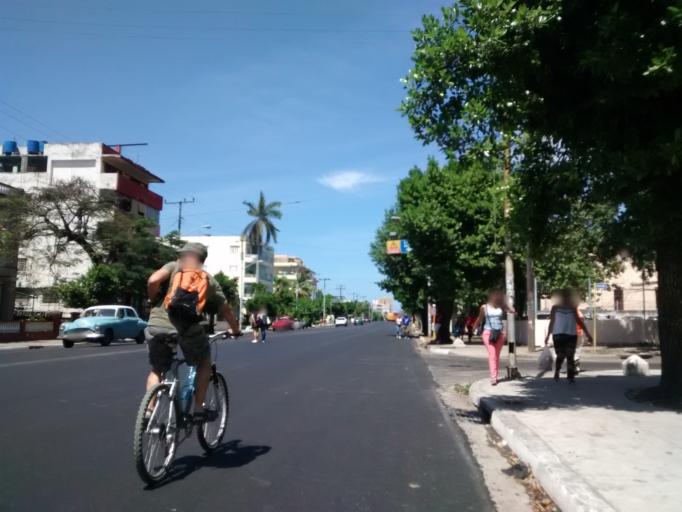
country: CU
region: La Habana
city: Havana
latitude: 23.1283
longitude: -82.3980
